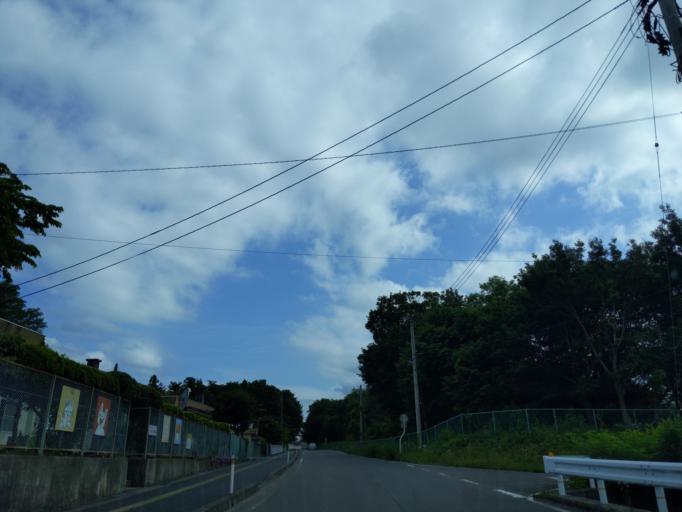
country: JP
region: Fukushima
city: Sukagawa
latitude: 37.2927
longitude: 140.3901
